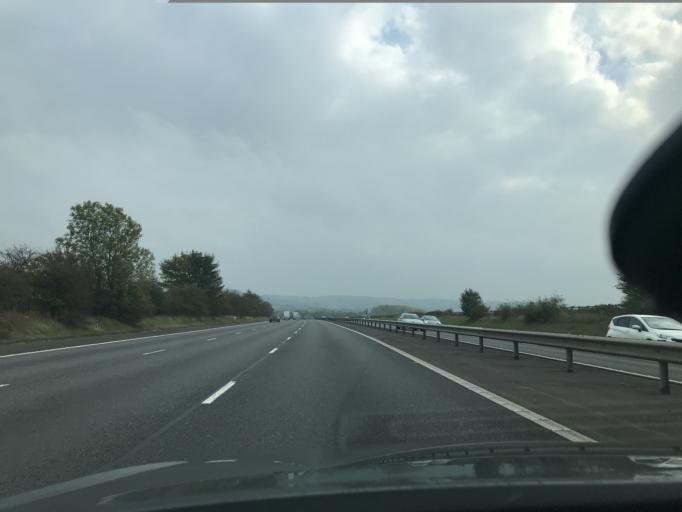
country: GB
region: England
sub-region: Oxfordshire
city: Watlington
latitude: 51.6870
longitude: -0.9770
